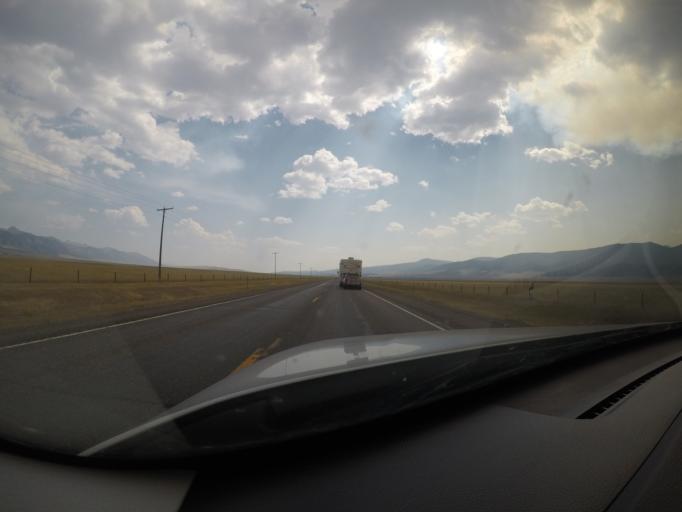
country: US
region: Montana
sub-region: Gallatin County
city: Big Sky
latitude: 45.0304
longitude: -111.6482
